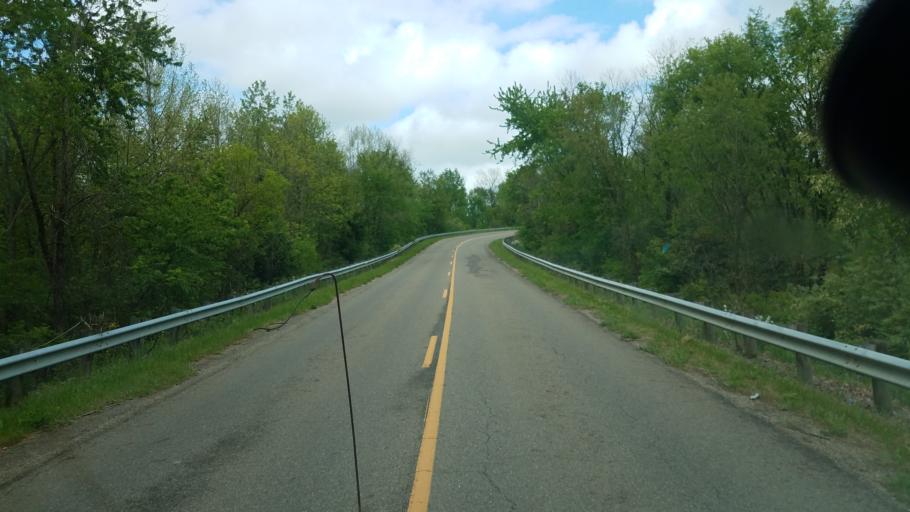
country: US
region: Ohio
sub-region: Tuscarawas County
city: Dover
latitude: 40.6090
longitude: -81.4259
